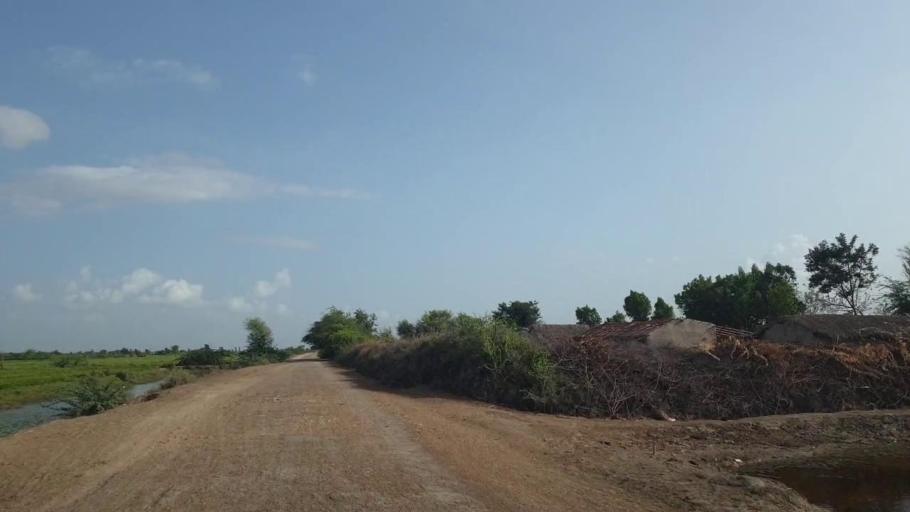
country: PK
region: Sindh
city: Kadhan
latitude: 24.6377
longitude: 69.0960
